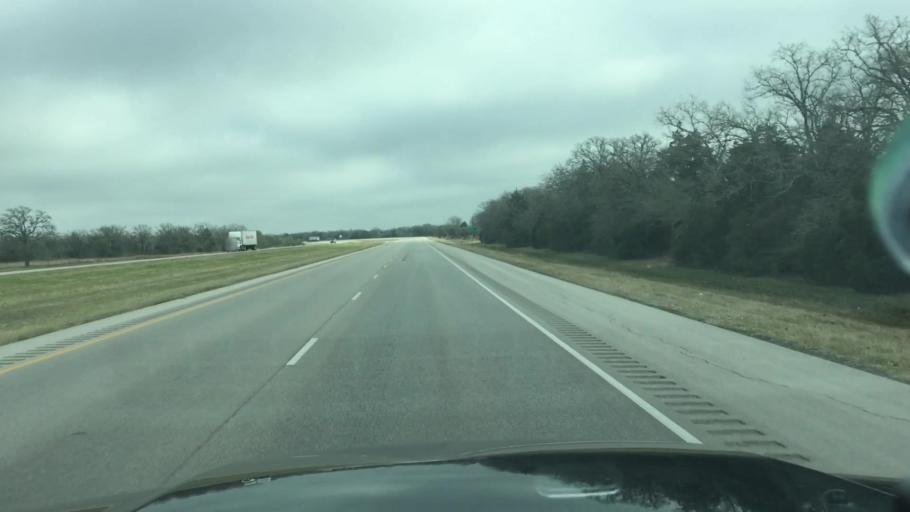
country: US
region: Texas
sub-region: Lee County
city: Giddings
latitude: 30.1427
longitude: -96.7713
